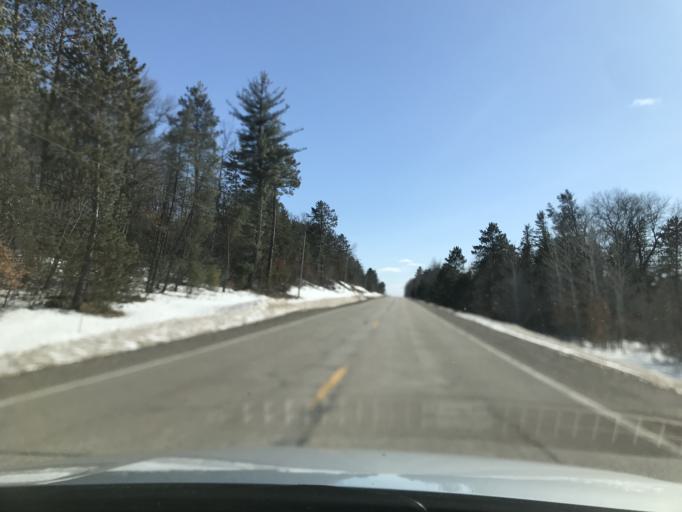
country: US
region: Wisconsin
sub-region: Marinette County
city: Niagara
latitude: 45.3617
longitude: -88.1007
